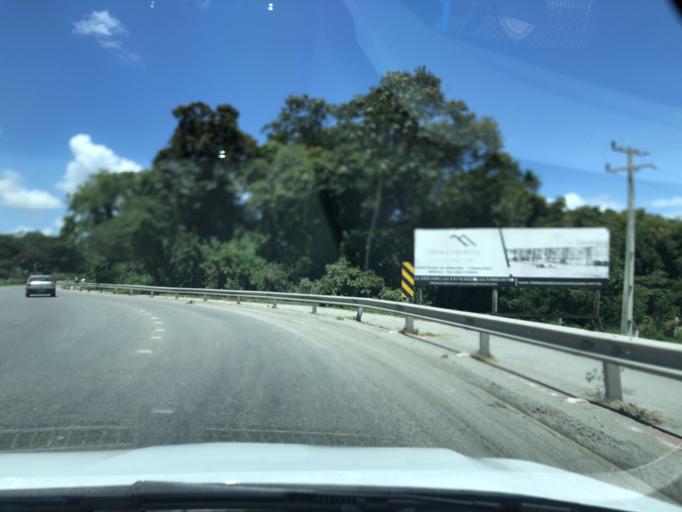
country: BR
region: Santa Catarina
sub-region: Sao Francisco Do Sul
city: Sao Francisco do Sul
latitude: -26.2509
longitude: -48.6101
